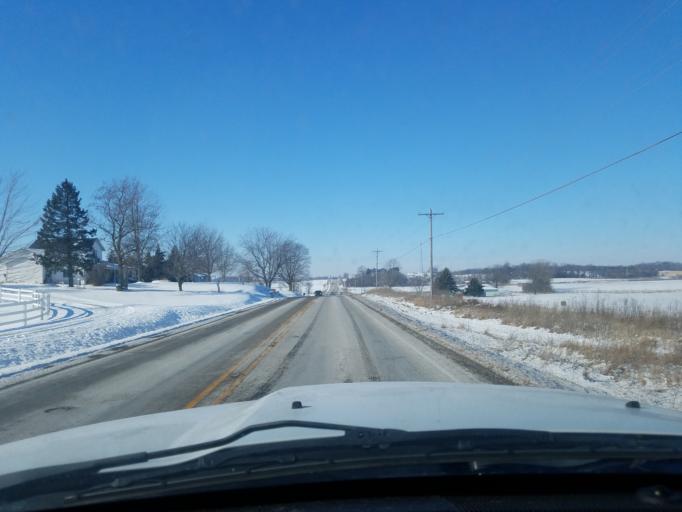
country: US
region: Indiana
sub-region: Noble County
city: Albion
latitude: 41.3958
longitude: -85.3813
